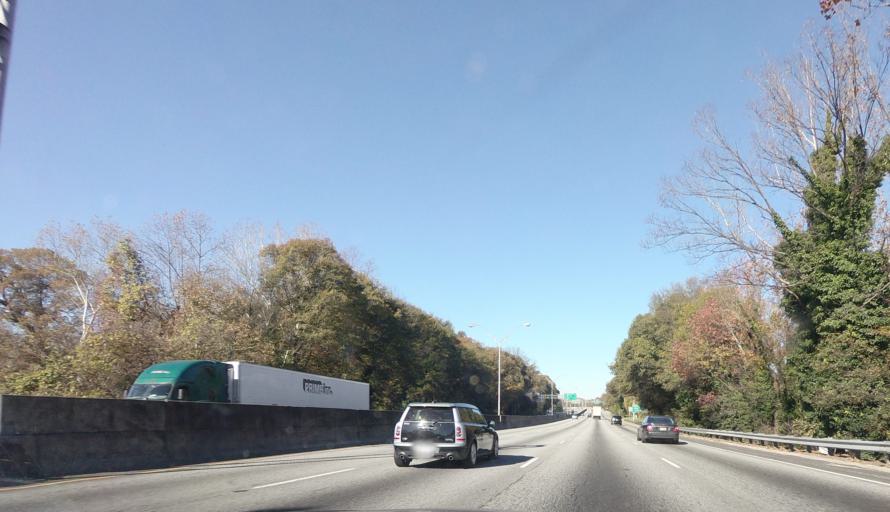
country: US
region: Georgia
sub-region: Fulton County
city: Atlanta
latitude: 33.7435
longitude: -84.4239
